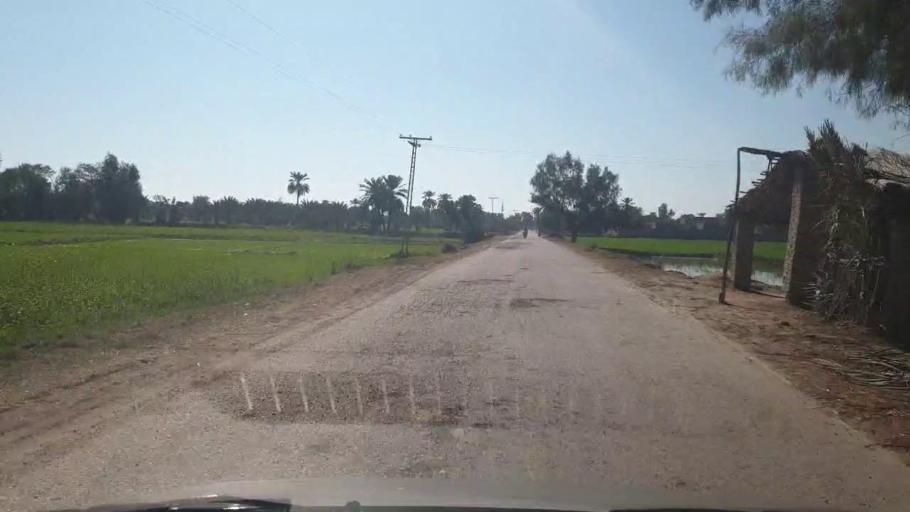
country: PK
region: Sindh
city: Bozdar
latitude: 27.1092
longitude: 68.6335
